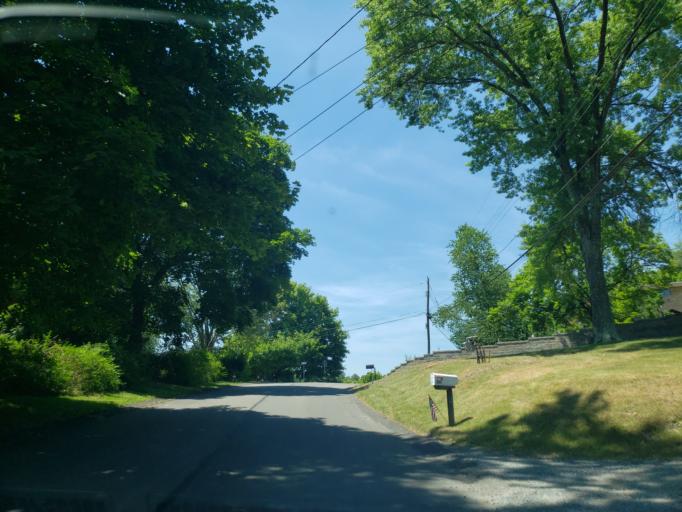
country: US
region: Pennsylvania
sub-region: Allegheny County
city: Emsworth
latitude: 40.5323
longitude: -80.0997
